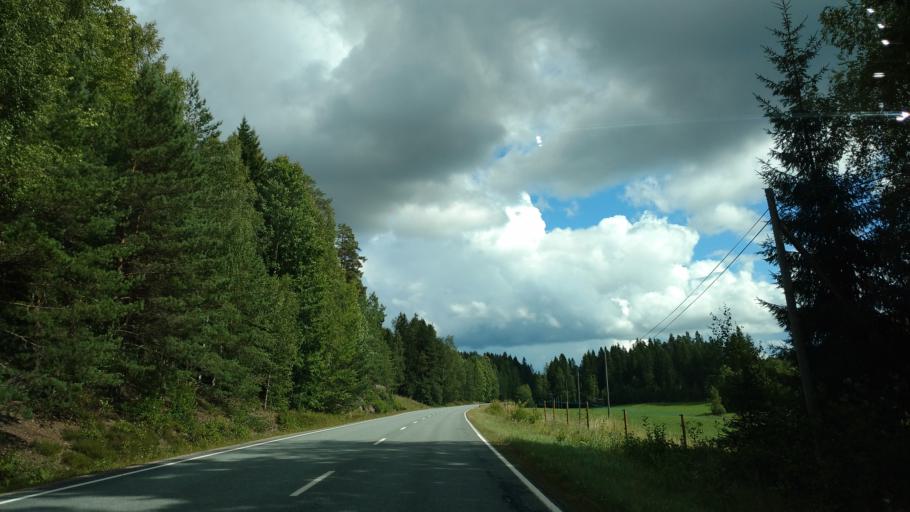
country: FI
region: Varsinais-Suomi
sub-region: Salo
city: Kisko
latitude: 60.2468
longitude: 23.5109
